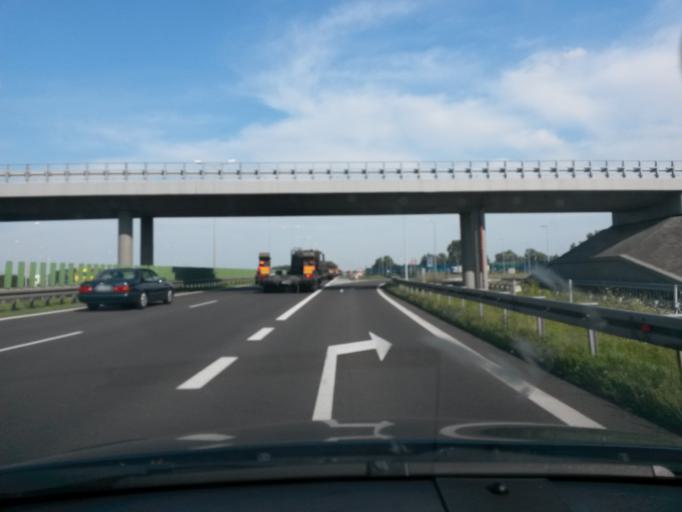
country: PL
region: Greater Poland Voivodeship
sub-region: Powiat wrzesinski
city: Kolaczkowo
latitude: 52.2951
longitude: 17.6494
